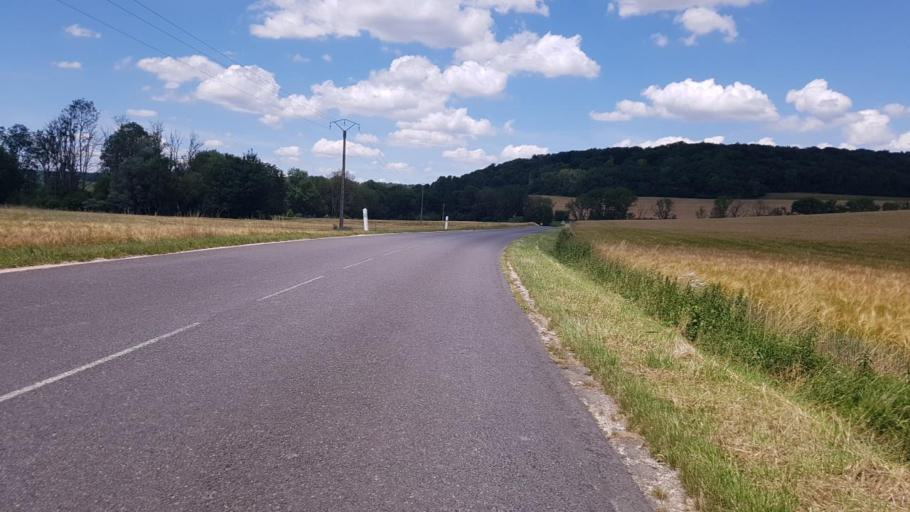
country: FR
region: Lorraine
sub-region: Departement de la Meuse
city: Ligny-en-Barrois
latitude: 48.6445
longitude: 5.4291
